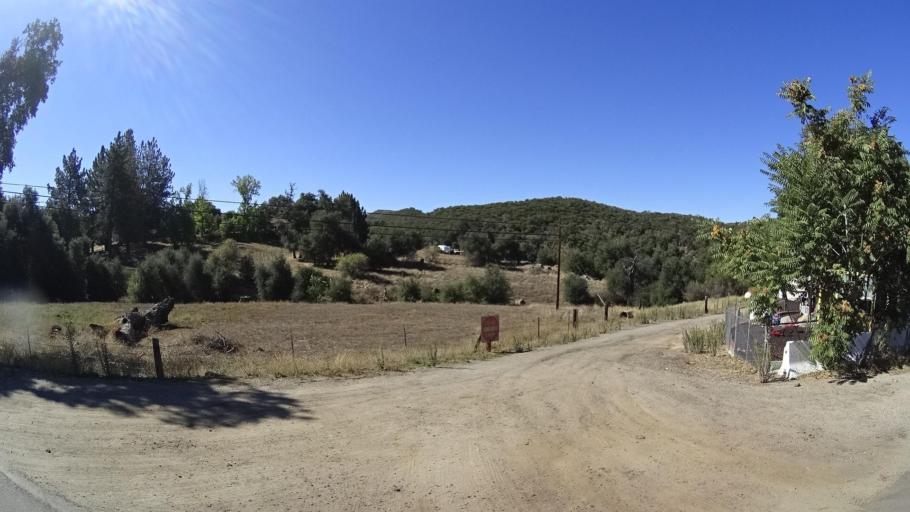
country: US
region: California
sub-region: San Diego County
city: Descanso
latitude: 32.8546
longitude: -116.6056
